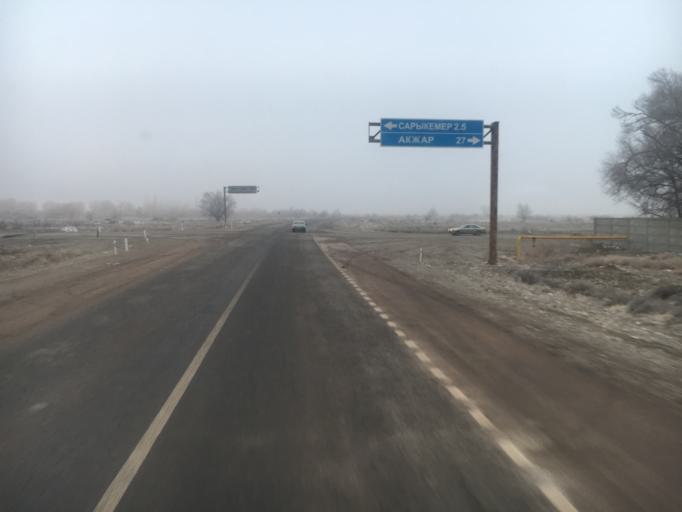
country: KZ
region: Zhambyl
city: Sarykemer
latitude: 43.0405
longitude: 71.5340
